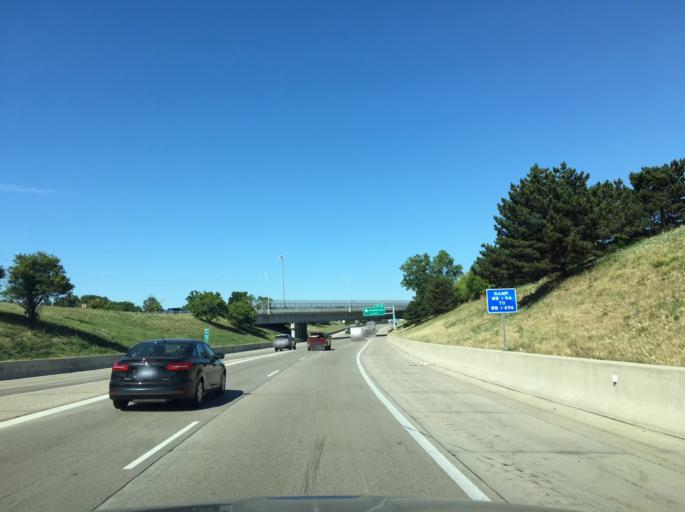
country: US
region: Michigan
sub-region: Macomb County
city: Roseville
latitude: 42.4960
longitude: -82.9218
